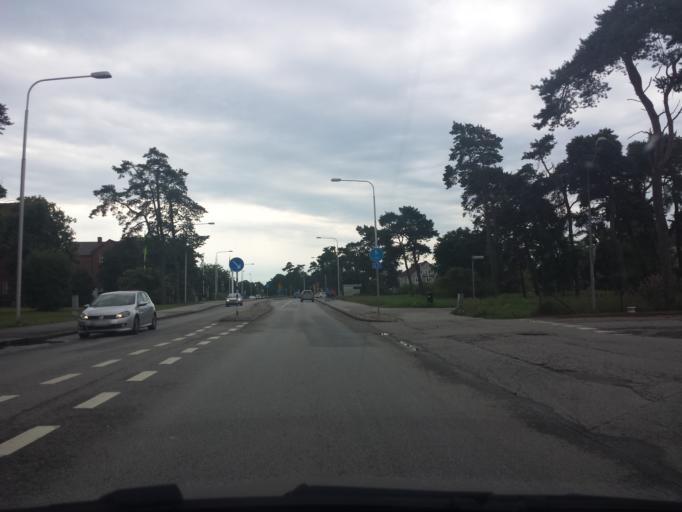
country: SE
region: Skane
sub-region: Ystads Kommun
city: Ystad
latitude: 55.4335
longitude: 13.8387
